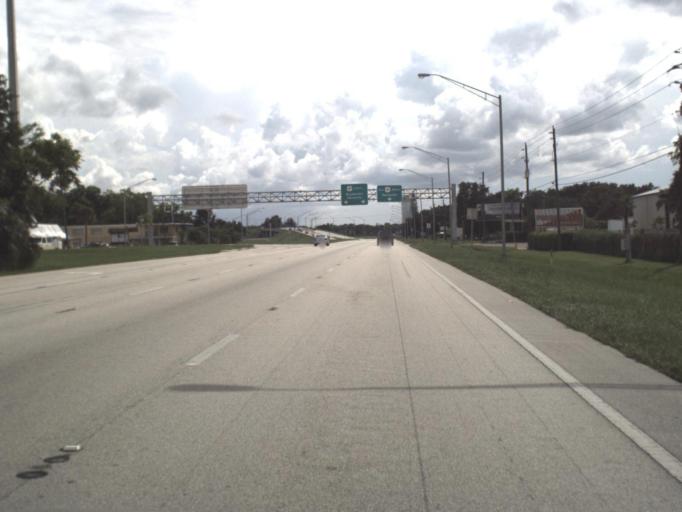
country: US
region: Florida
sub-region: Manatee County
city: Memphis
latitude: 27.5470
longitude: -82.5647
